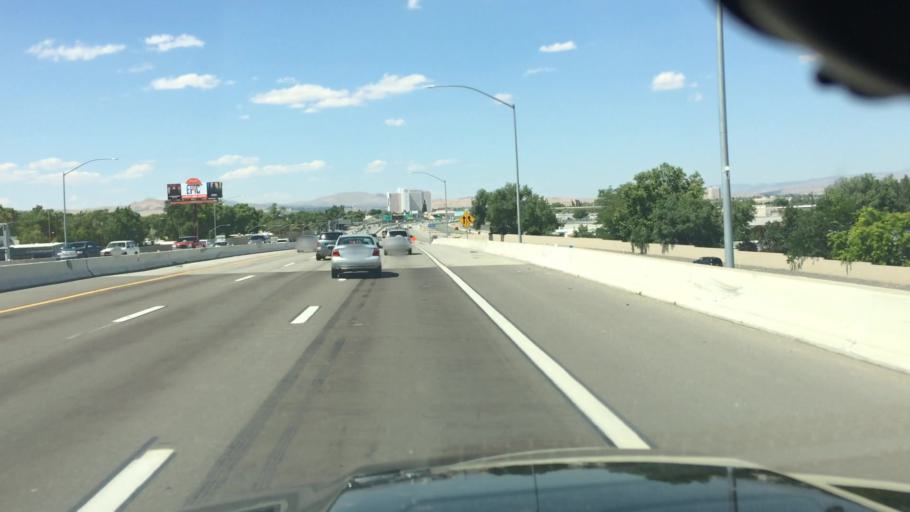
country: US
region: Nevada
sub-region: Washoe County
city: Reno
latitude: 39.4929
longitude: -119.7845
